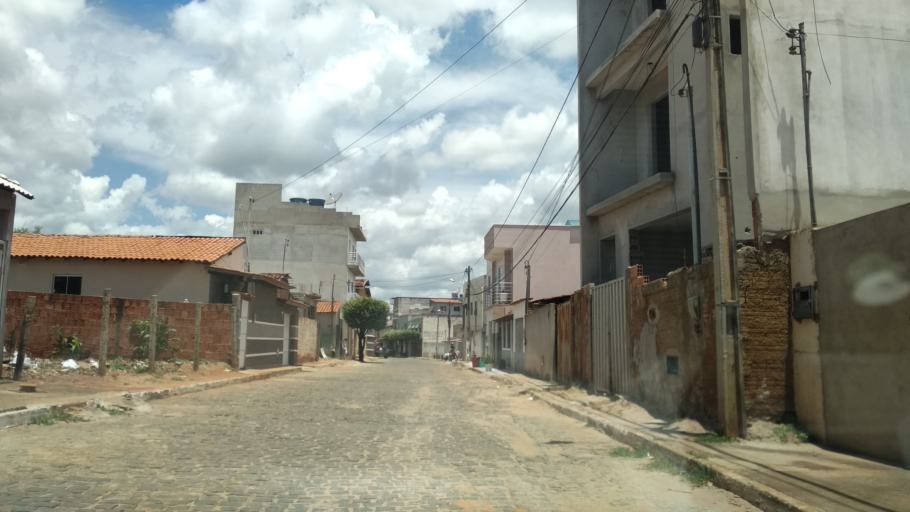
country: BR
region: Bahia
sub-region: Caetite
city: Caetite
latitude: -14.0599
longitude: -42.4829
